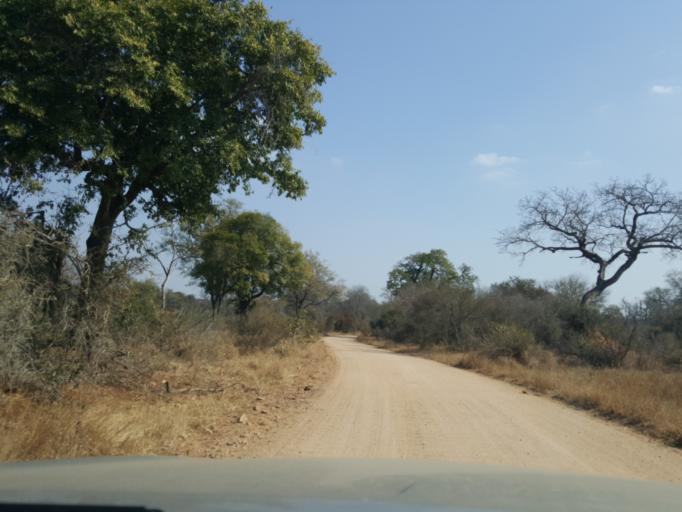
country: ZA
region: Mpumalanga
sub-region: Ehlanzeni District
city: Komatipoort
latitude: -25.2892
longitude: 31.7697
